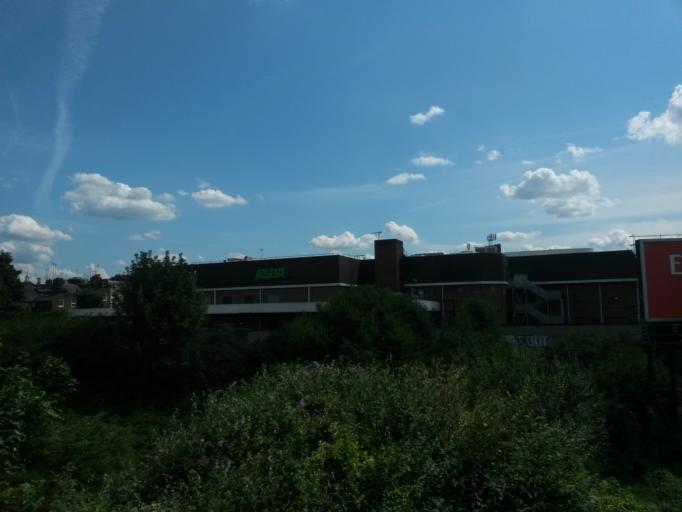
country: GB
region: England
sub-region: Greater London
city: Battersea
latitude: 51.4664
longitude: -0.1657
